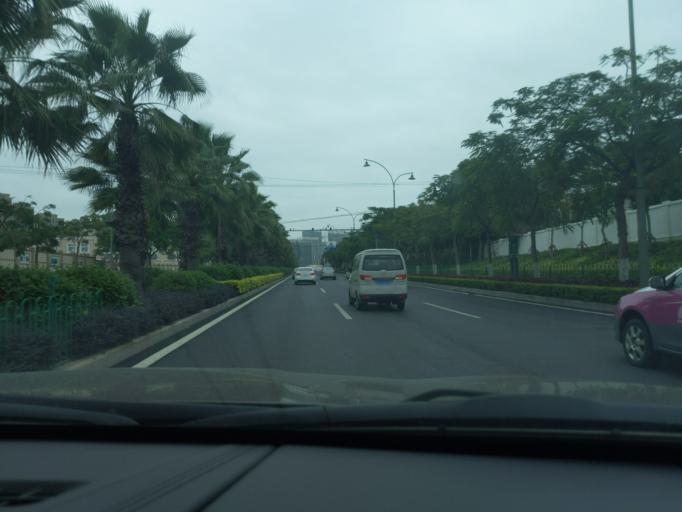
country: CN
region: Fujian
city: Liuwudian
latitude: 24.4981
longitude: 118.1709
